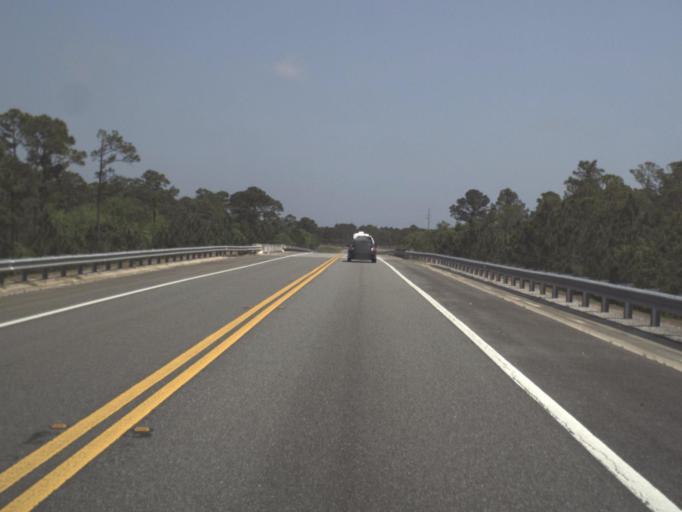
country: US
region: Florida
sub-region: Santa Rosa County
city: Tiger Point
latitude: 30.3976
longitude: -87.0742
